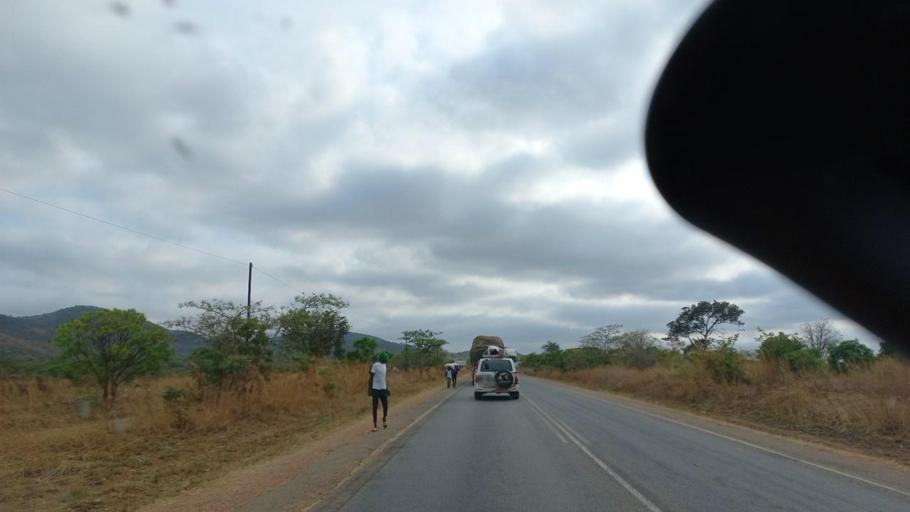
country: ZM
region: Lusaka
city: Chongwe
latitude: -15.2395
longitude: 29.1651
